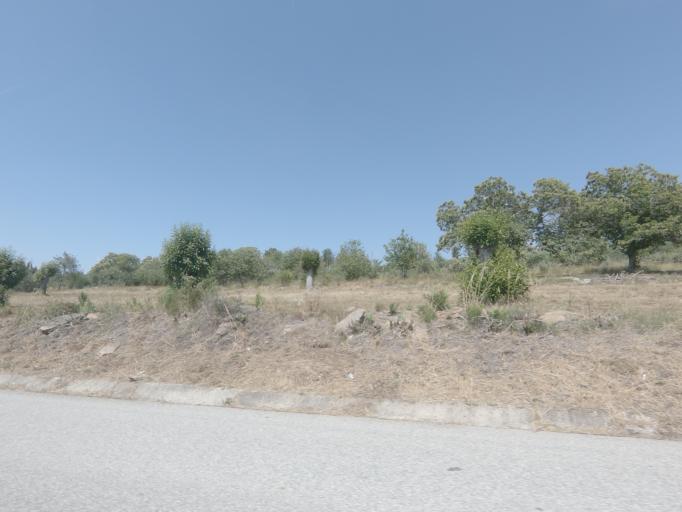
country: PT
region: Viseu
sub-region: Tarouca
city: Tarouca
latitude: 40.9896
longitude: -7.8098
